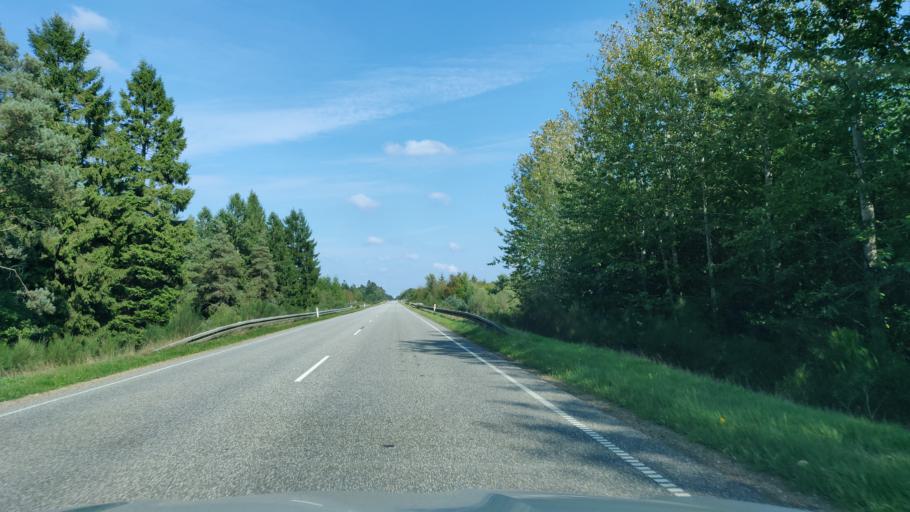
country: DK
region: Central Jutland
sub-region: Herning Kommune
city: Sunds
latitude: 56.3643
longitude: 8.9778
